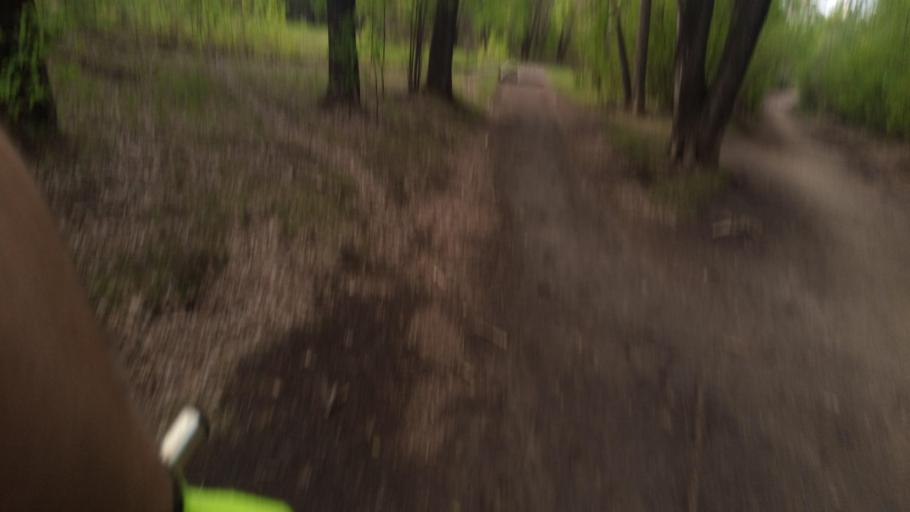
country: RU
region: Chelyabinsk
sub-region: Gorod Chelyabinsk
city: Chelyabinsk
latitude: 55.1674
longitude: 61.3417
